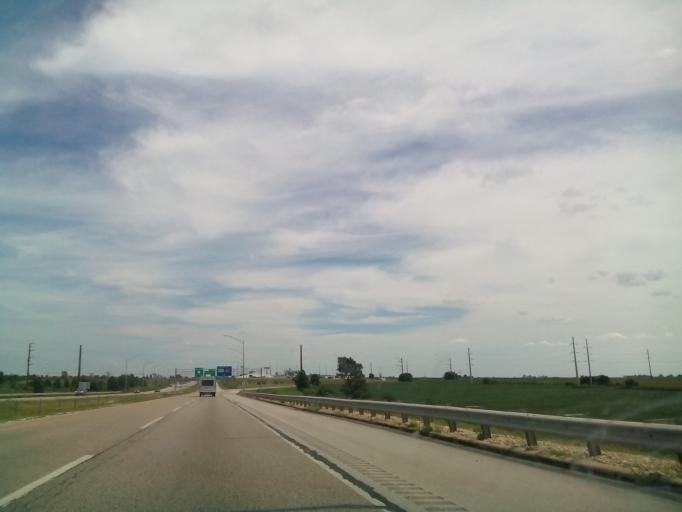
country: US
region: Illinois
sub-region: DeKalb County
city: DeKalb
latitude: 41.9023
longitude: -88.7485
